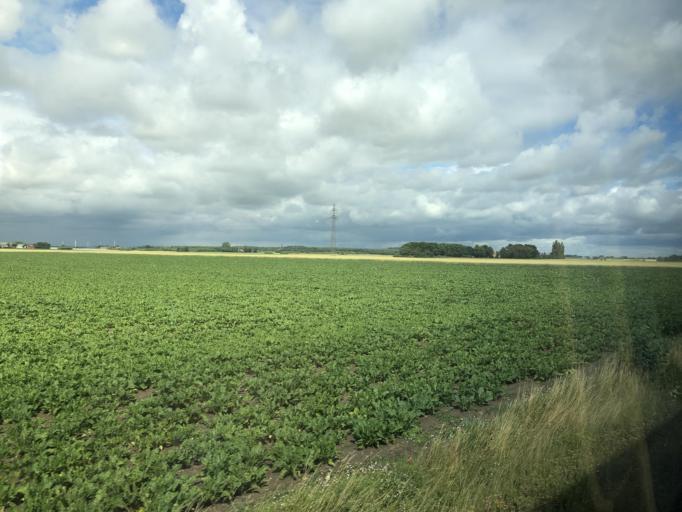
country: SE
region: Skane
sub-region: Landskrona
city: Asmundtorp
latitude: 55.8597
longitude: 12.9219
